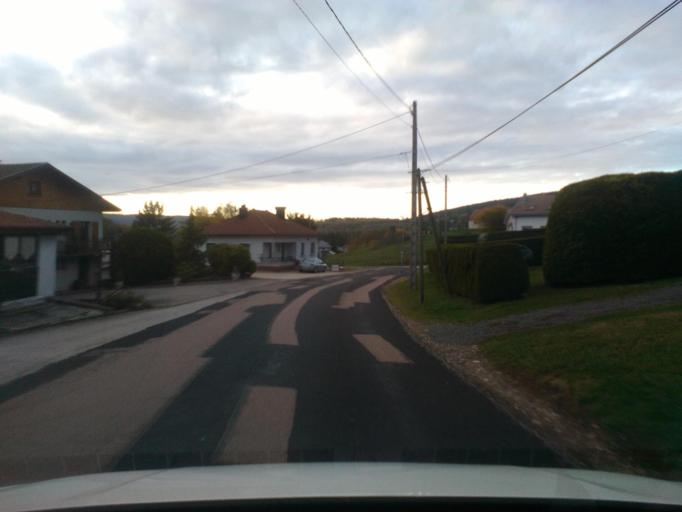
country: FR
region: Lorraine
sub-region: Departement des Vosges
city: Fraize
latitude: 48.1878
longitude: 7.0062
